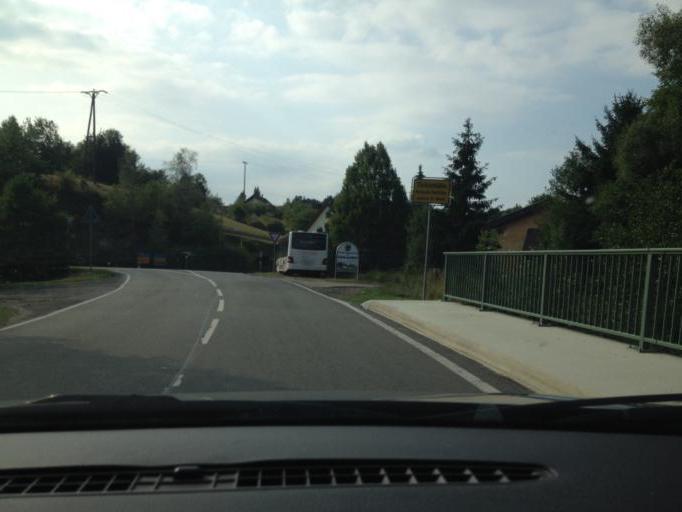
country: DE
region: Saarland
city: Nohfelden
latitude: 49.5751
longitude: 7.1124
